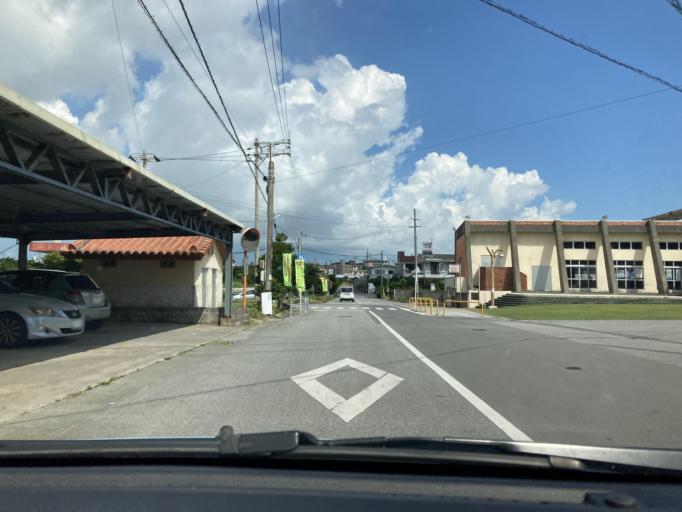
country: JP
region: Okinawa
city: Tomigusuku
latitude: 26.1527
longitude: 127.7543
